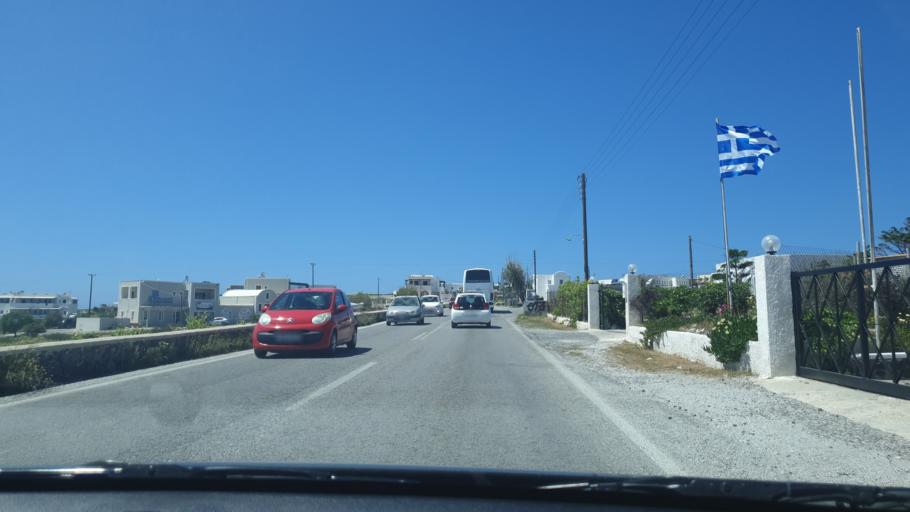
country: GR
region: South Aegean
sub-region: Nomos Kykladon
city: Emporeio
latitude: 36.3653
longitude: 25.4293
